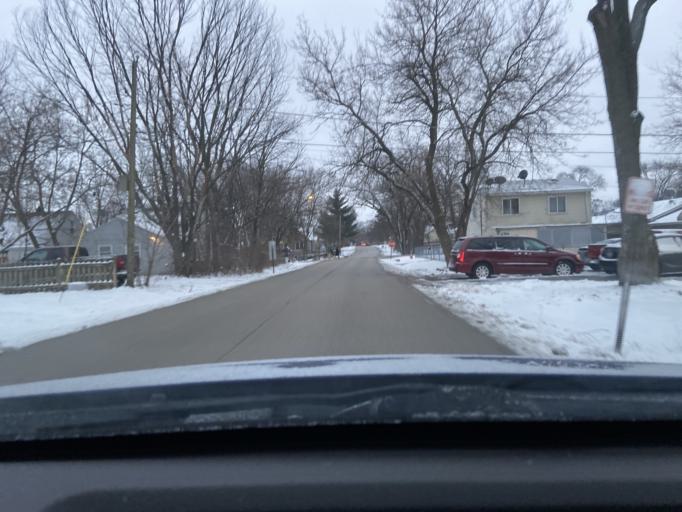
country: US
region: Illinois
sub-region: Lake County
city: Round Lake Park
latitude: 42.3521
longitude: -88.0767
